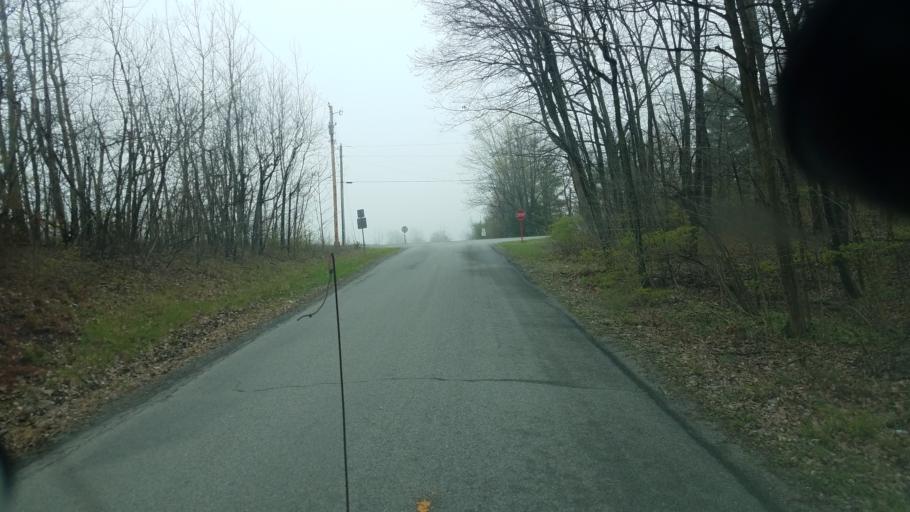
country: US
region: Ohio
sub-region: Logan County
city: Northwood
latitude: 40.4336
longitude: -83.7569
